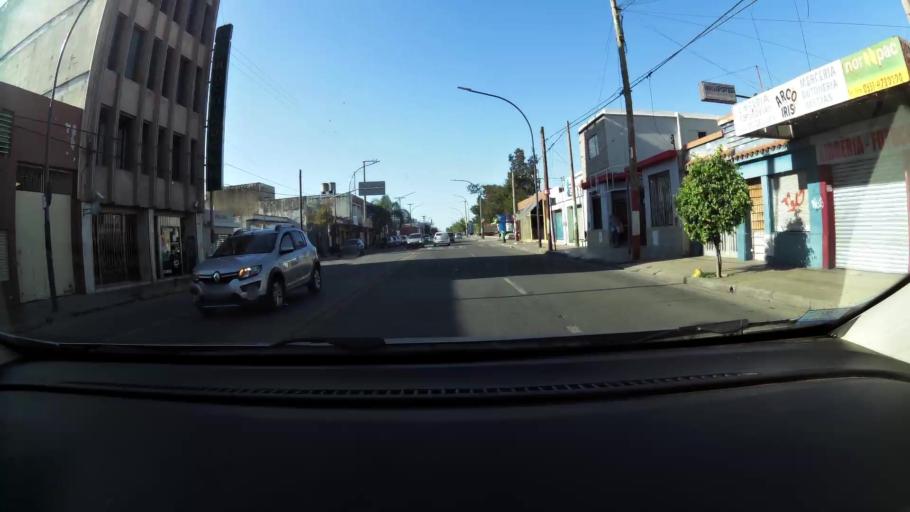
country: AR
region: Cordoba
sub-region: Departamento de Capital
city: Cordoba
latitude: -31.3850
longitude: -64.1760
